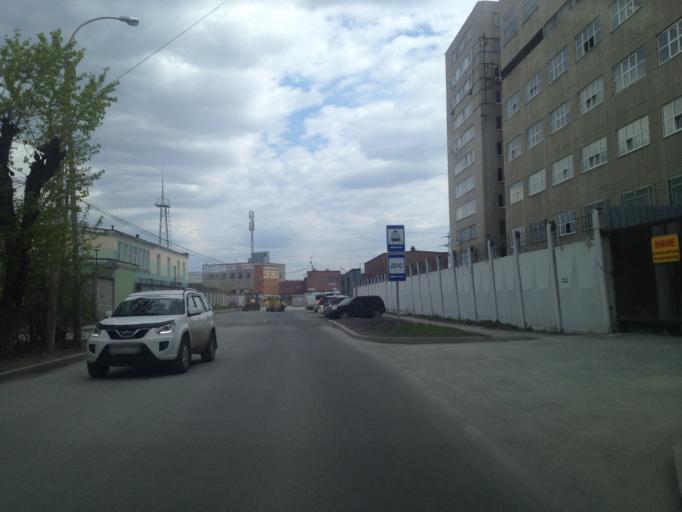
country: RU
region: Sverdlovsk
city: Yekaterinburg
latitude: 56.8541
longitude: 60.6668
